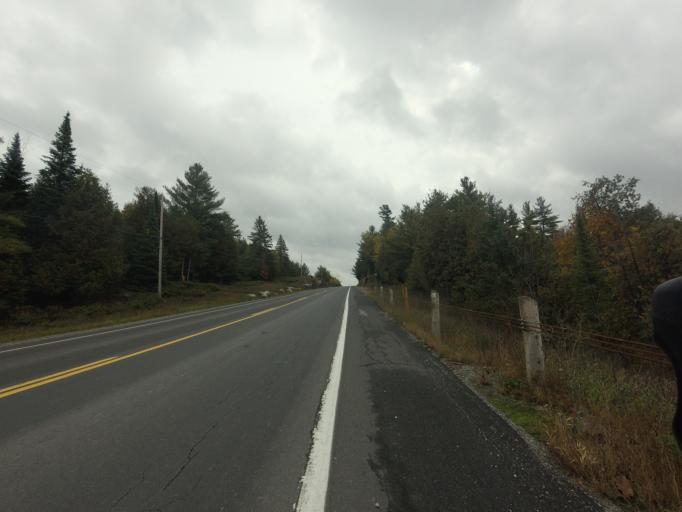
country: CA
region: Ontario
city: Perth
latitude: 45.1103
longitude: -76.4807
